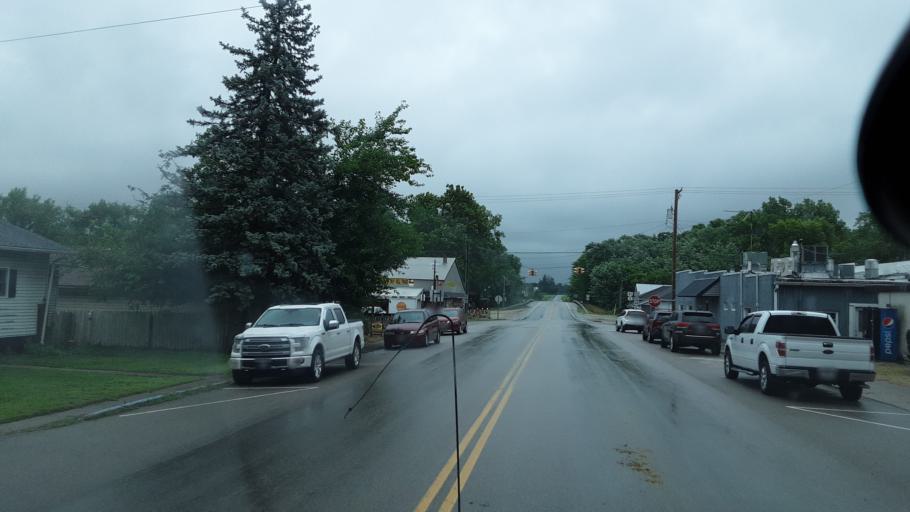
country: US
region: Ohio
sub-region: Mercer County
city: Rockford
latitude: 40.7484
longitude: -84.7913
